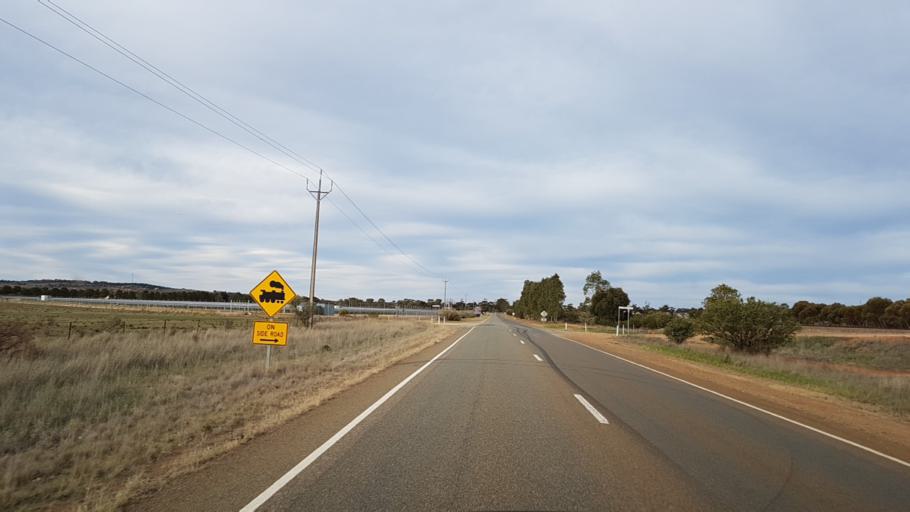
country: AU
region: South Australia
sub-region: Peterborough
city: Peterborough
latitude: -32.9816
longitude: 138.8124
